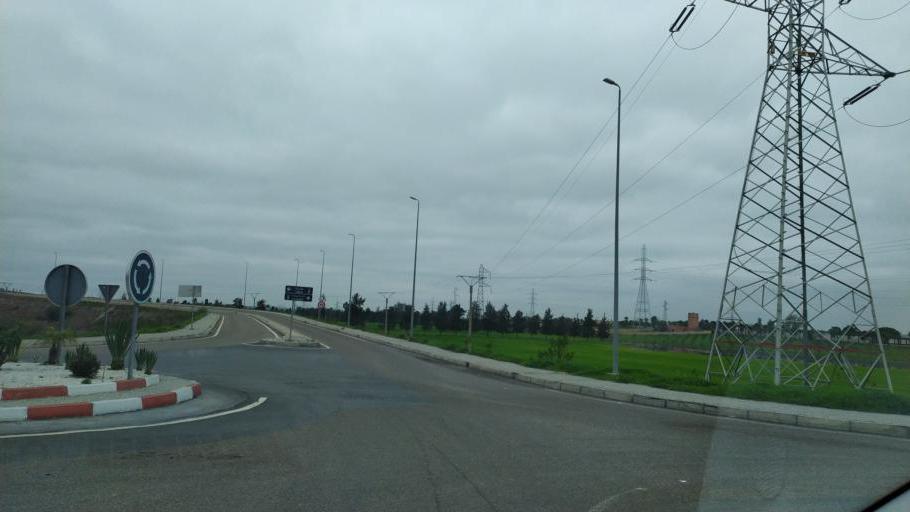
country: MA
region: Rabat-Sale-Zemmour-Zaer
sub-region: Rabat
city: Rabat
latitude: 33.9067
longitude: -6.7767
